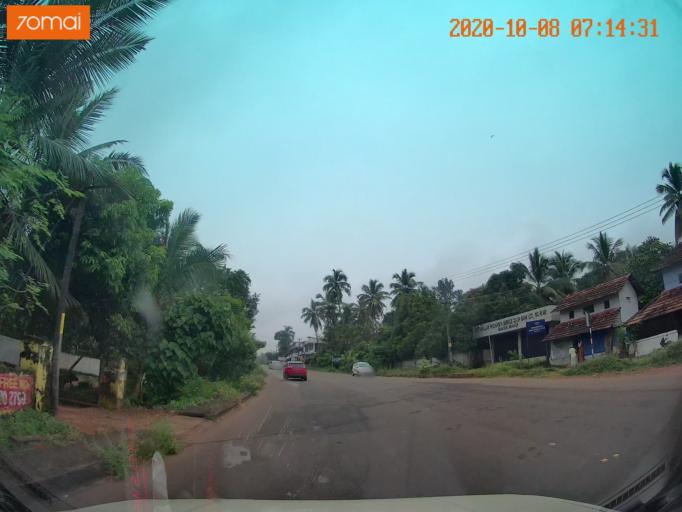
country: IN
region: Kerala
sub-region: Malappuram
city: Ponnani
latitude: 10.8180
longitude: 76.0190
